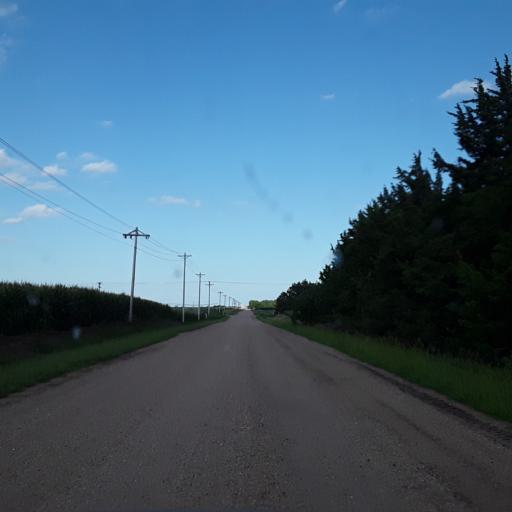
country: US
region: Nebraska
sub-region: Hall County
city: Wood River
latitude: 40.9168
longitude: -98.5535
